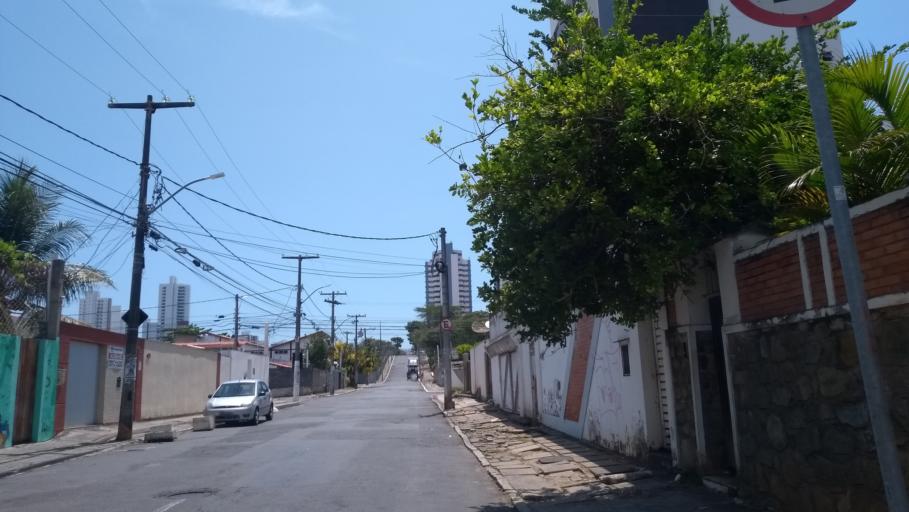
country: BR
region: Bahia
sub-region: Salvador
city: Salvador
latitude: -12.9915
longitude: -38.4604
